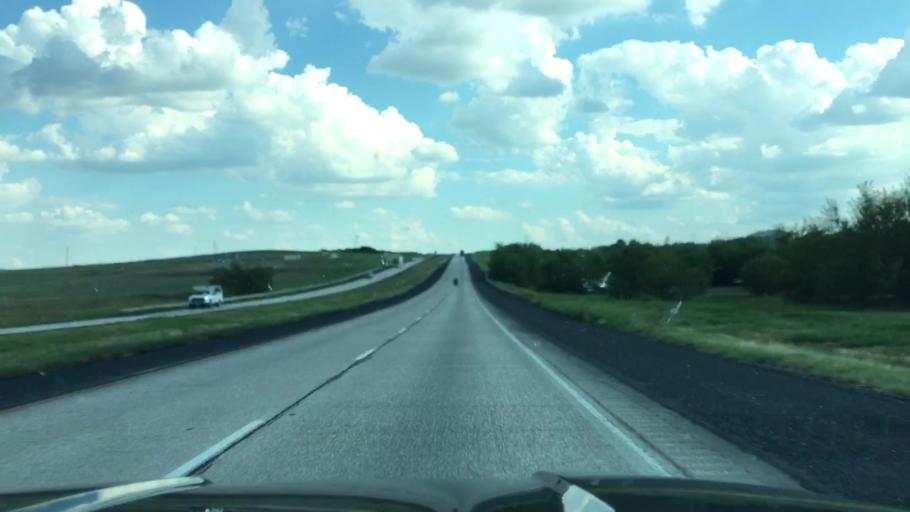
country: US
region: Texas
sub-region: Wise County
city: New Fairview
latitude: 33.1366
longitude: -97.4959
